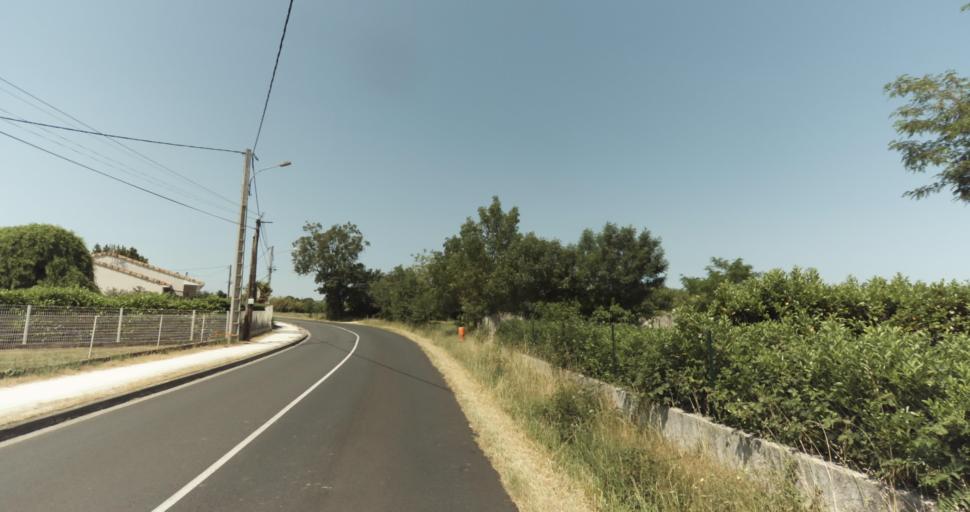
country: FR
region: Midi-Pyrenees
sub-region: Departement de la Haute-Garonne
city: La Salvetat-Saint-Gilles
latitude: 43.5679
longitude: 1.2775
